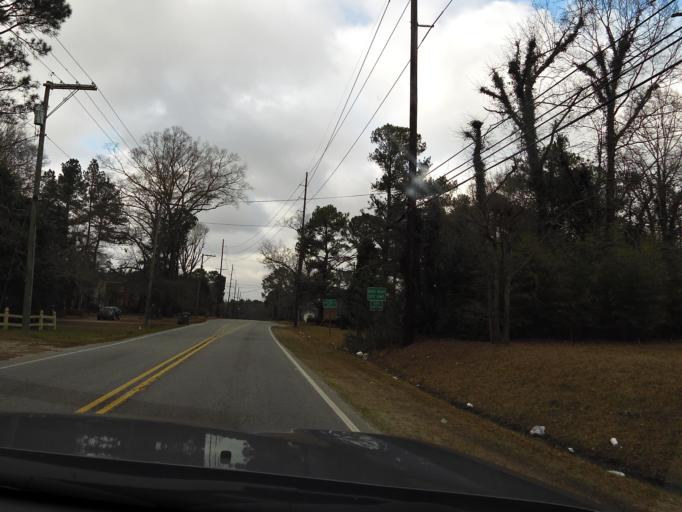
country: US
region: North Carolina
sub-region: Nash County
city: Rocky Mount
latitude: 35.9167
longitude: -77.7879
